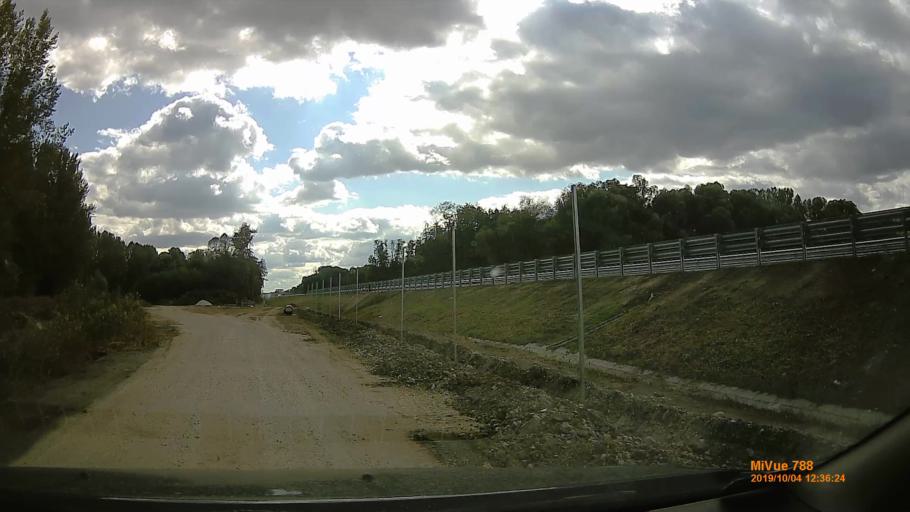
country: HU
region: Somogy
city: Karad
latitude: 46.6760
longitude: 17.7786
